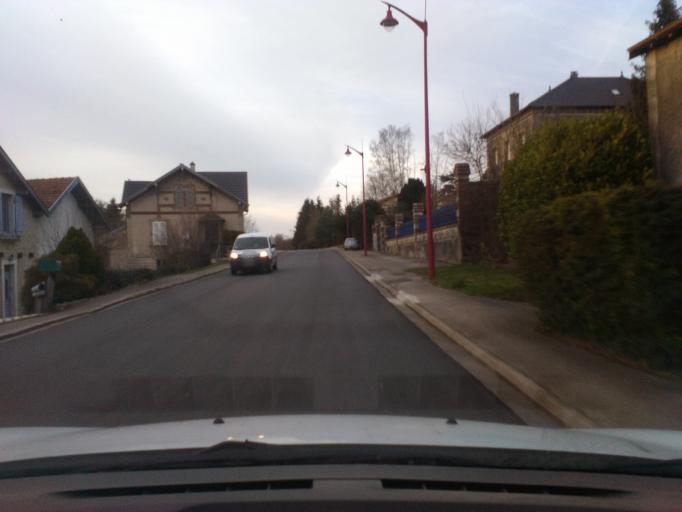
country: FR
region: Lorraine
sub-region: Departement des Vosges
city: Vincey
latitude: 48.3611
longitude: 6.3244
